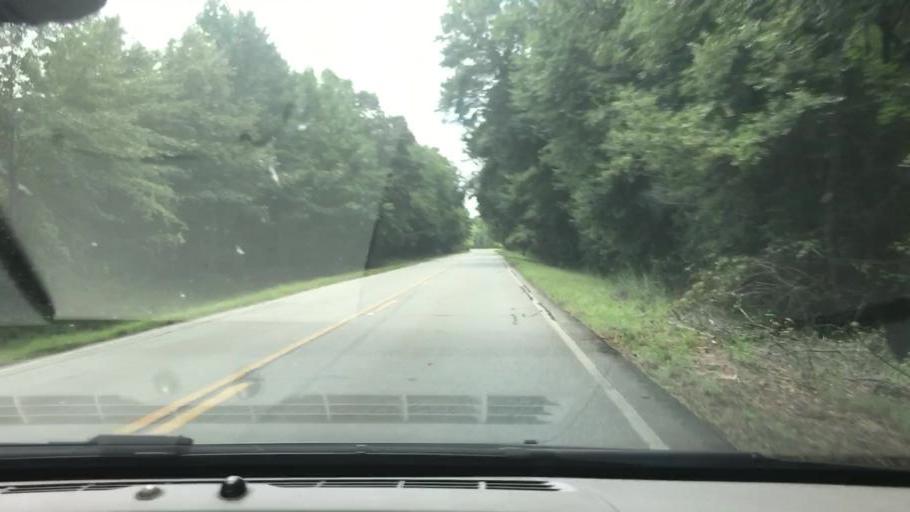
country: US
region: Georgia
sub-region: Quitman County
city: Georgetown
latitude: 32.0955
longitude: -85.0397
